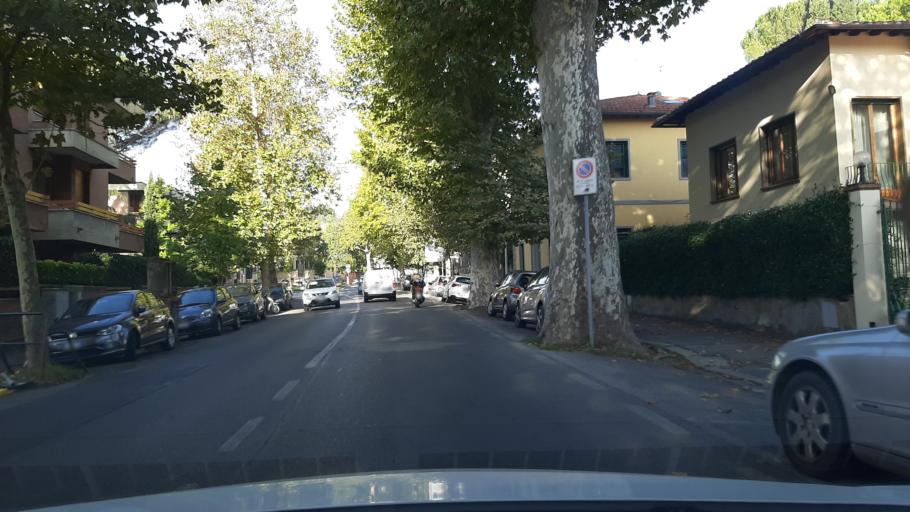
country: IT
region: Tuscany
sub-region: Province of Florence
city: Fiesole
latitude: 43.7869
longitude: 11.2858
